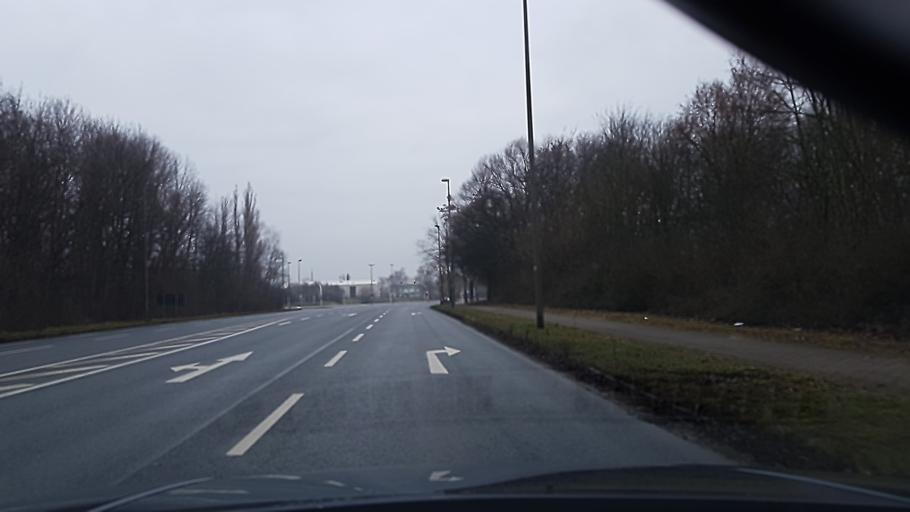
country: DE
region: Lower Saxony
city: Cramme
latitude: 52.1471
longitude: 10.4155
